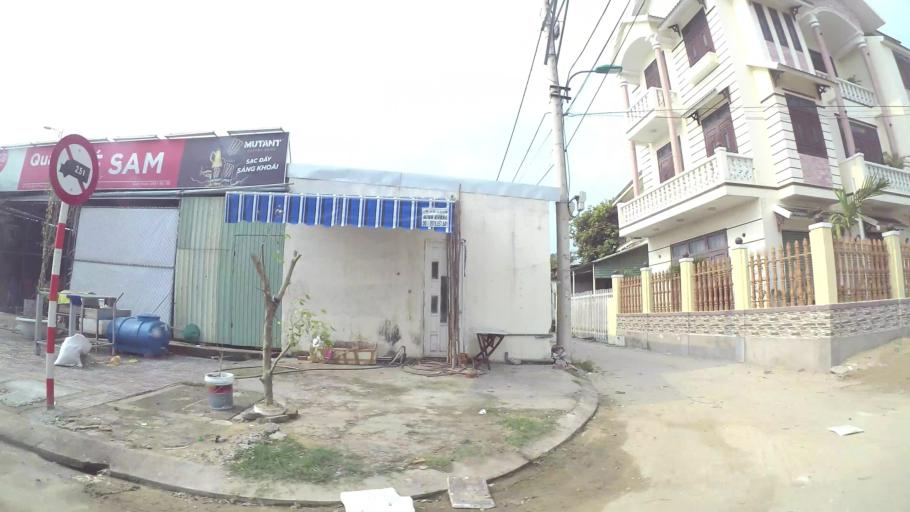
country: VN
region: Da Nang
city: Son Tra
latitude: 16.0886
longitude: 108.2488
